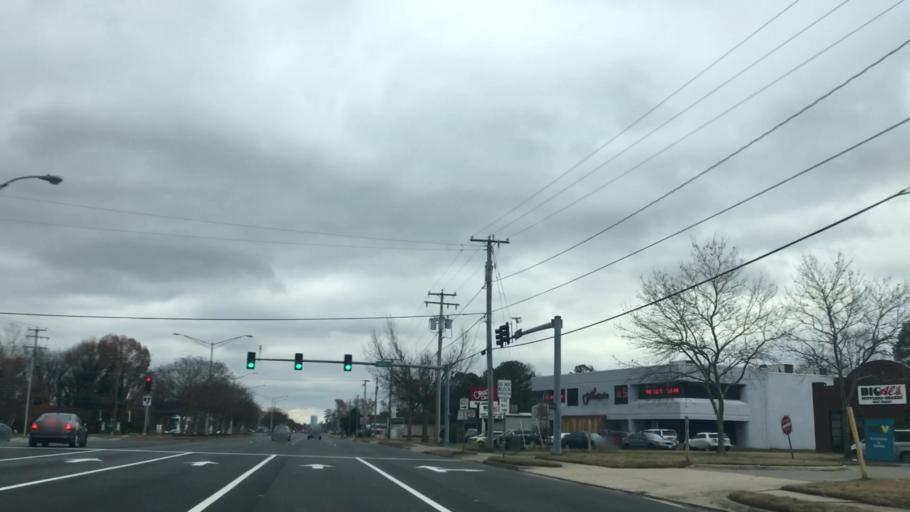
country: US
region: Virginia
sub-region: City of Chesapeake
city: Chesapeake
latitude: 36.8521
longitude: -76.1724
